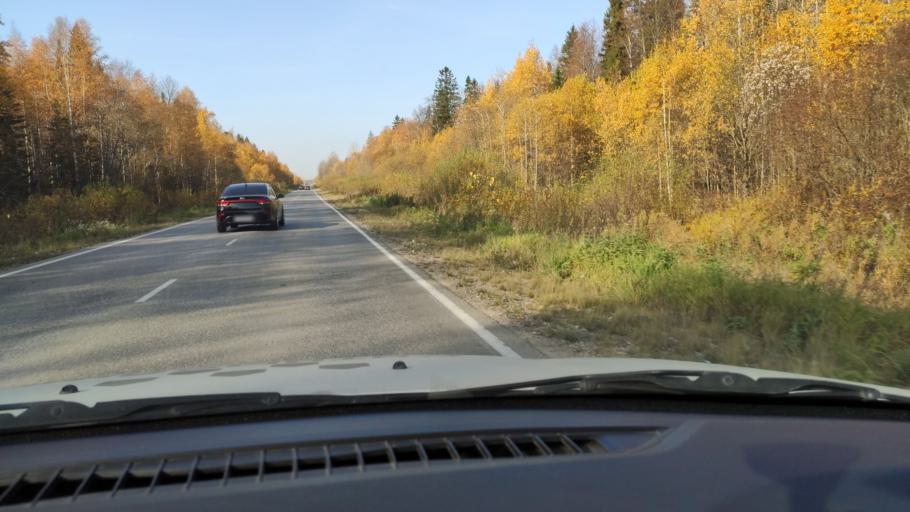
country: RU
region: Perm
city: Novyye Lyady
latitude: 58.0255
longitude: 56.6342
